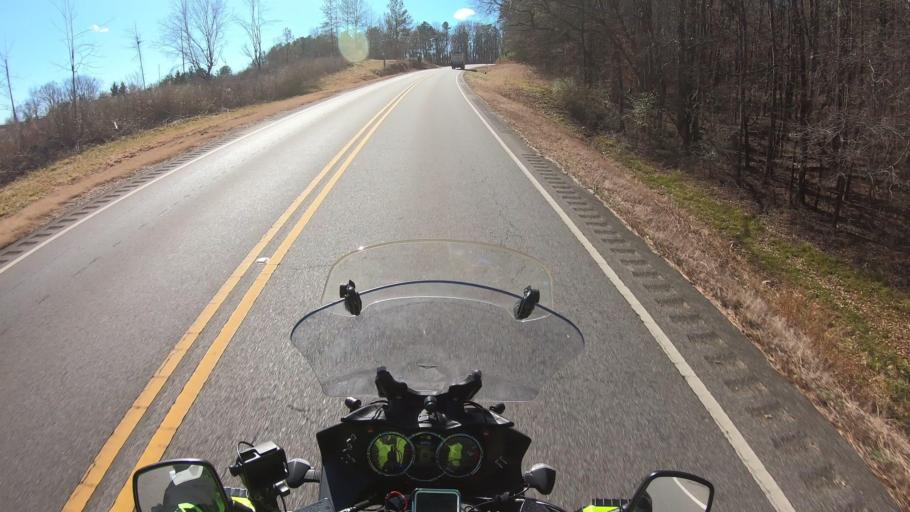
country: US
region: Alabama
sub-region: Cleburne County
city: Heflin
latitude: 33.5159
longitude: -85.6446
